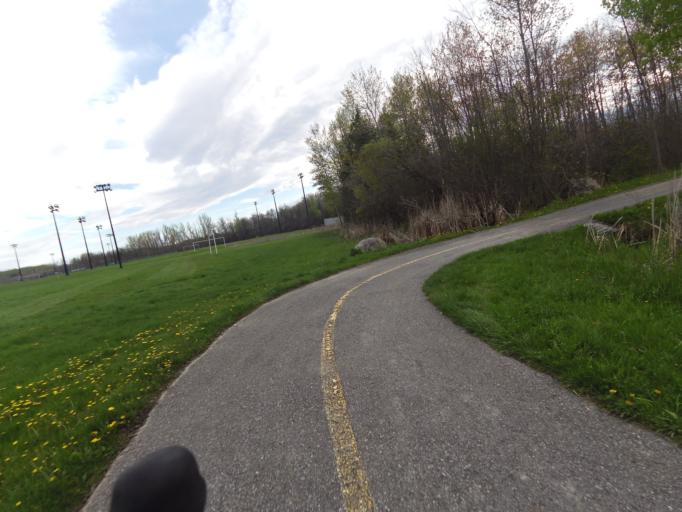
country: CA
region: Ontario
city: Bells Corners
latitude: 45.2765
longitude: -75.7952
